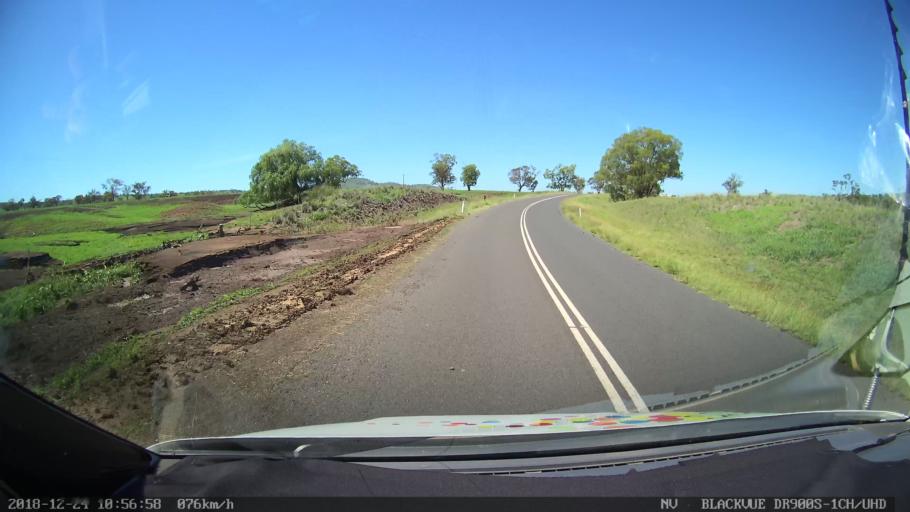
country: AU
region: New South Wales
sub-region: Upper Hunter Shire
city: Merriwa
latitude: -32.0313
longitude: 150.4165
